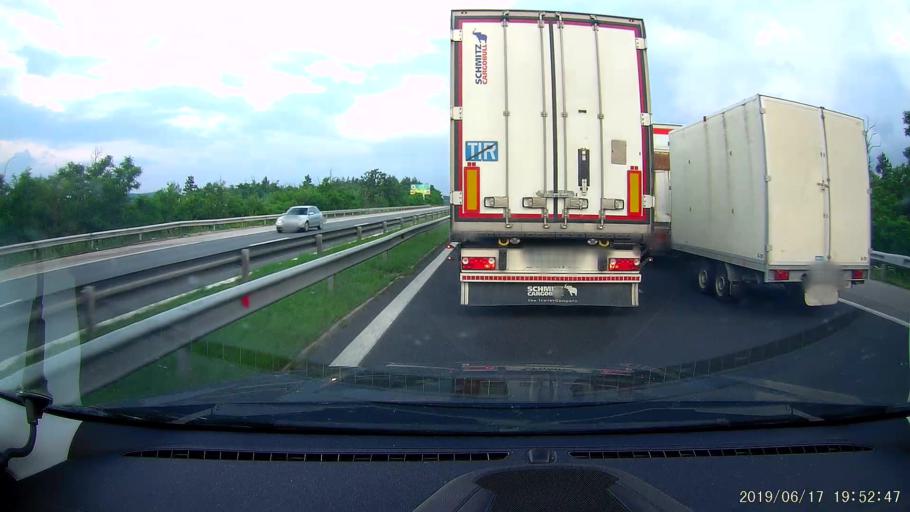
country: BG
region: Sofiya
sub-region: Obshtina Ikhtiman
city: Ikhtiman
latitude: 42.5330
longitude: 23.7348
